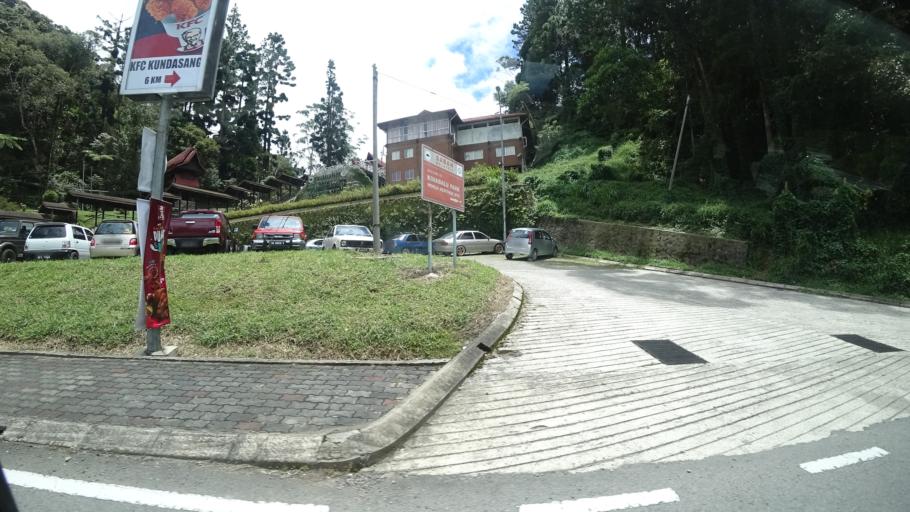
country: MY
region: Sabah
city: Ranau
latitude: 6.0050
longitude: 116.5422
